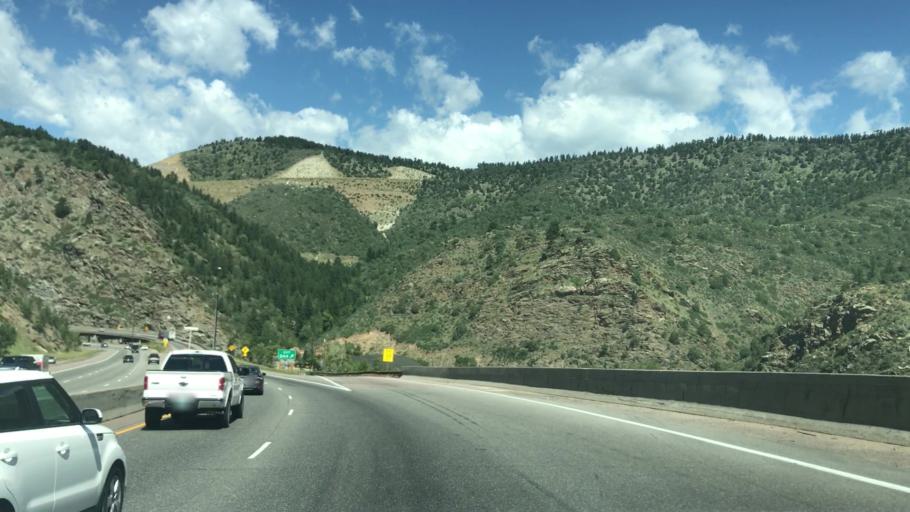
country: US
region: Colorado
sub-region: Clear Creek County
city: Idaho Springs
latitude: 39.7440
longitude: -105.4338
